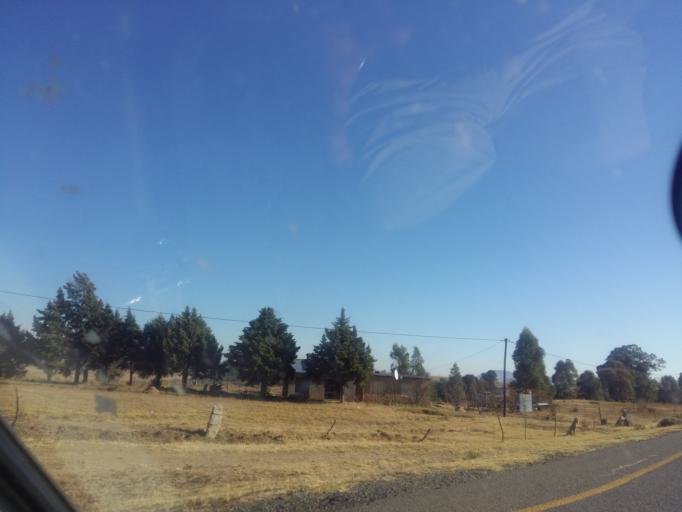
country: LS
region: Mafeteng
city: Mafeteng
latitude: -29.7754
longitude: 27.2831
